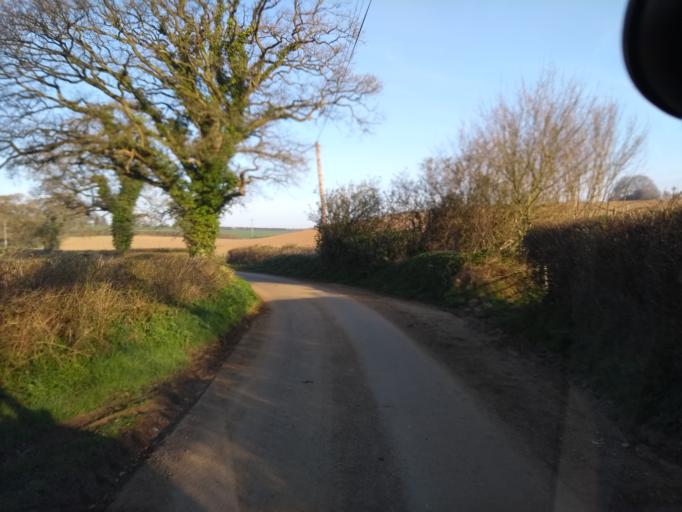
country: GB
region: England
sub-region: Somerset
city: Crewkerne
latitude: 50.8350
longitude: -2.7877
